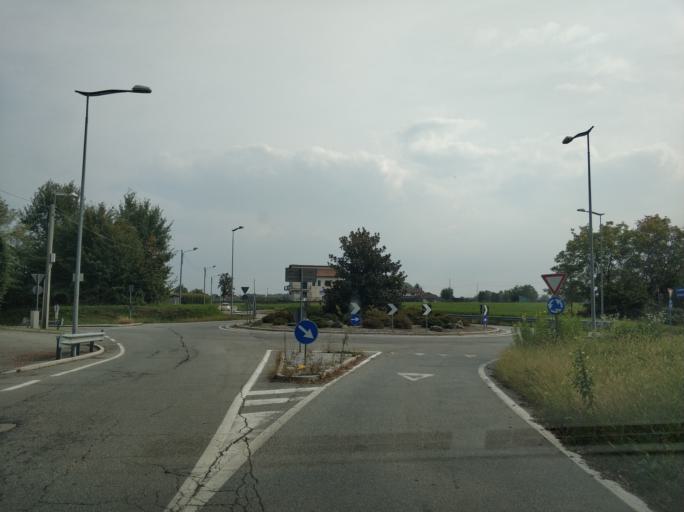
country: IT
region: Piedmont
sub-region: Provincia di Torino
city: San Carlo Canavese
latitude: 45.2435
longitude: 7.6250
